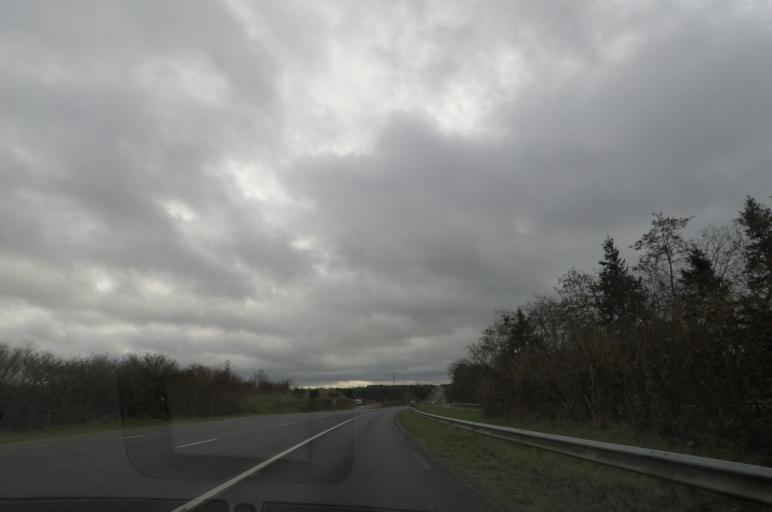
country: FR
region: Centre
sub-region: Departement du Loir-et-Cher
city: Saint-Sulpice-de-Pommeray
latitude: 47.6573
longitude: 1.2697
